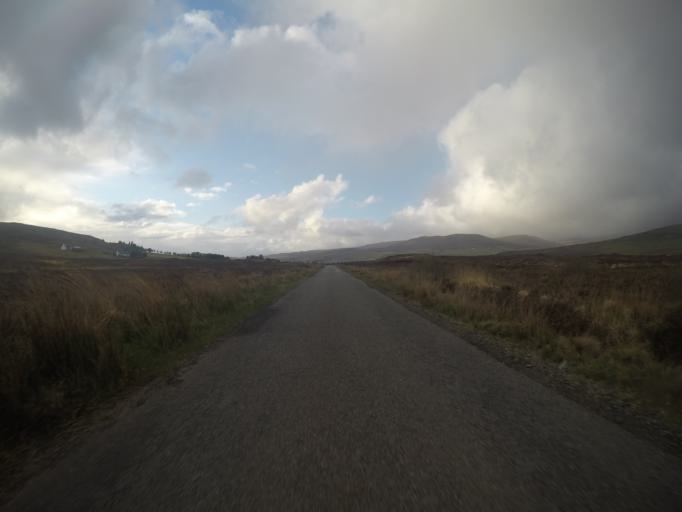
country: GB
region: Scotland
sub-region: Highland
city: Isle of Skye
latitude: 57.4626
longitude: -6.2968
